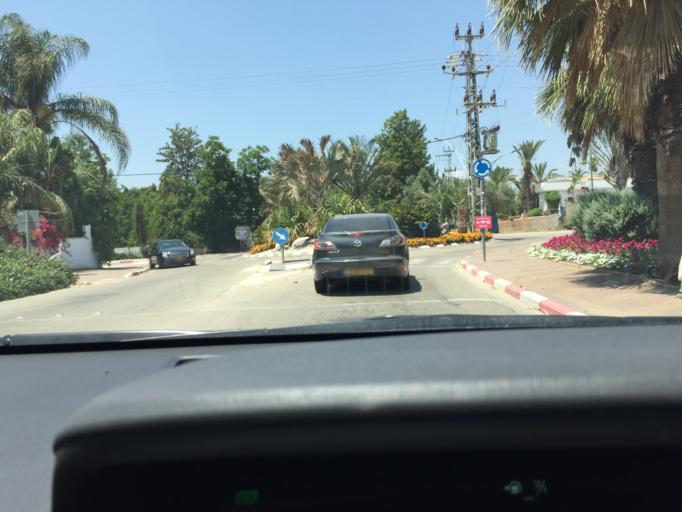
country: IL
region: Central District
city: Nehalim
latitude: 32.0508
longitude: 34.9029
